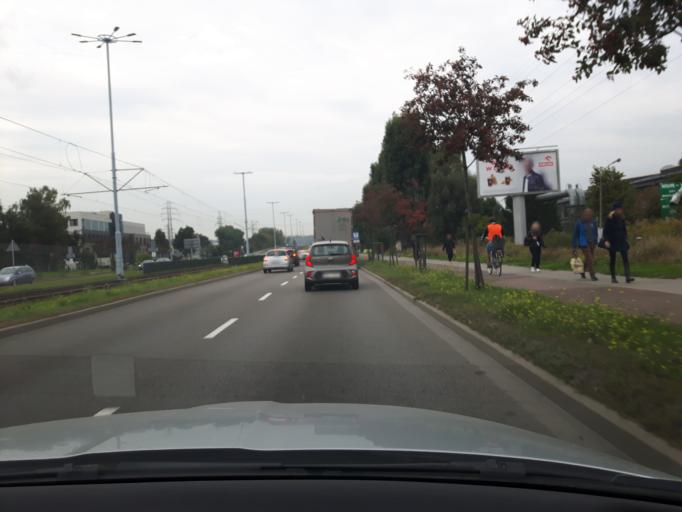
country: PL
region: Pomeranian Voivodeship
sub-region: Gdansk
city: Gdansk
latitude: 54.3833
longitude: 18.6395
